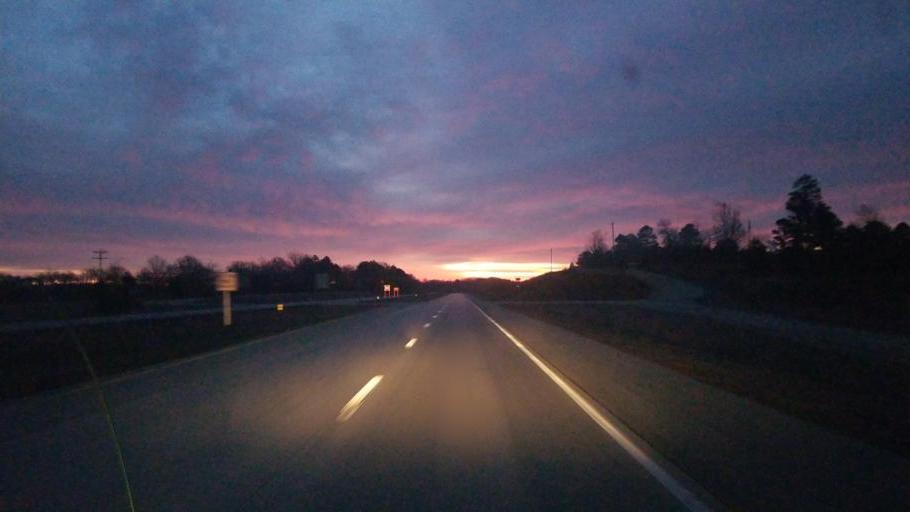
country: US
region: Missouri
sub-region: Shannon County
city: Winona
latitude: 36.9984
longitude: -91.4652
